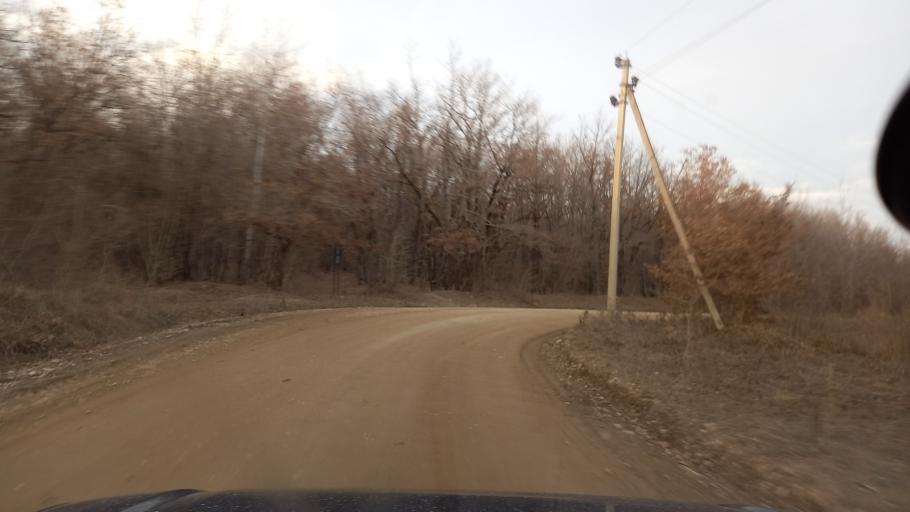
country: RU
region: Adygeya
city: Kamennomostskiy
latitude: 44.2051
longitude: 40.2495
